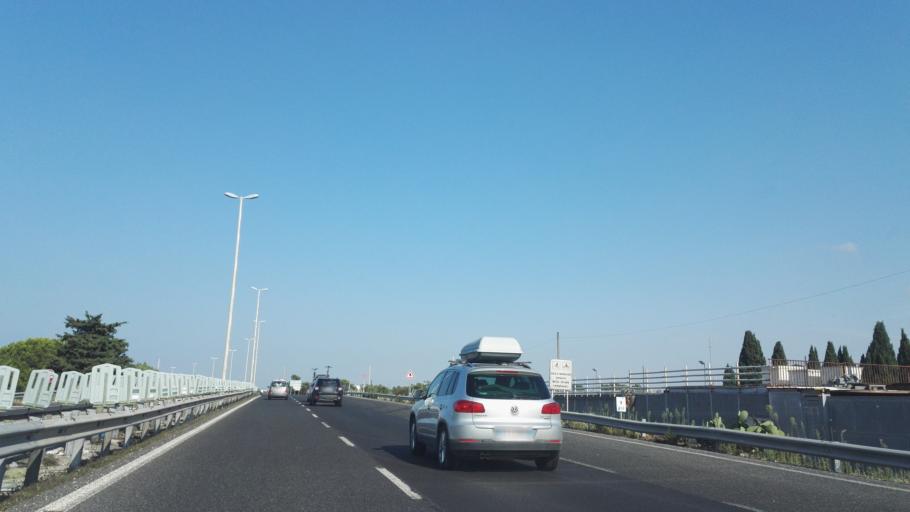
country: IT
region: Apulia
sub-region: Provincia di Bari
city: Parco Scizzo-Parchitello
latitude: 41.0828
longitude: 17.0030
